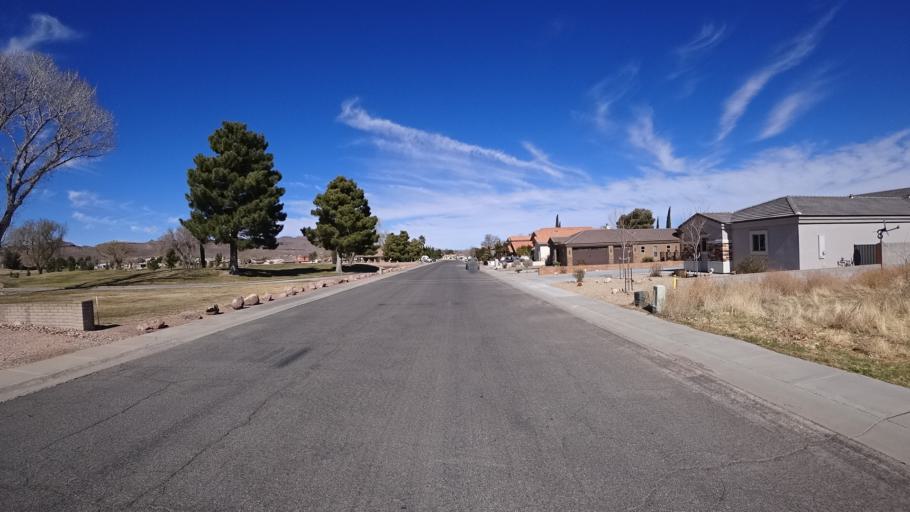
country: US
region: Arizona
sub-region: Mohave County
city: Kingman
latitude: 35.2084
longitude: -114.0414
